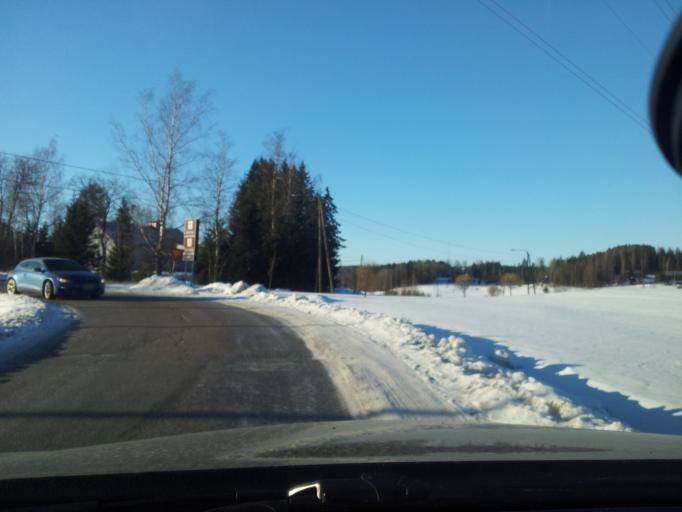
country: FI
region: Uusimaa
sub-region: Helsinki
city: Vihti
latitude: 60.3786
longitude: 24.3577
